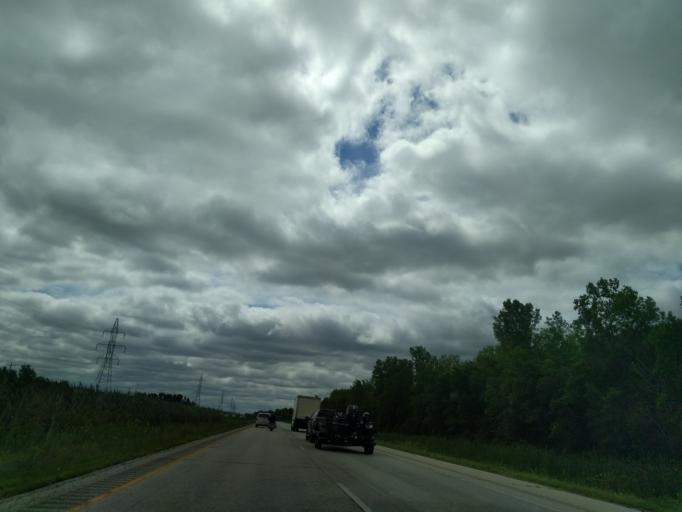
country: US
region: Wisconsin
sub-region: Brown County
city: Suamico
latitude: 44.6112
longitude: -88.0503
